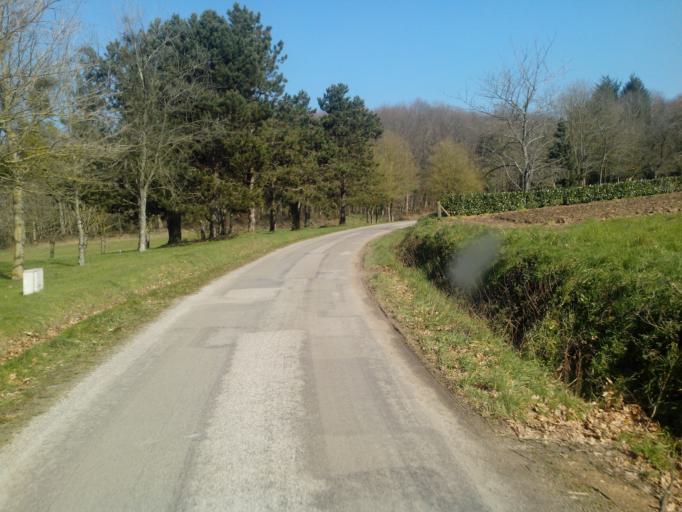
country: FR
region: Brittany
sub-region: Departement du Morbihan
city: Meneac
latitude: 48.1332
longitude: -2.4752
